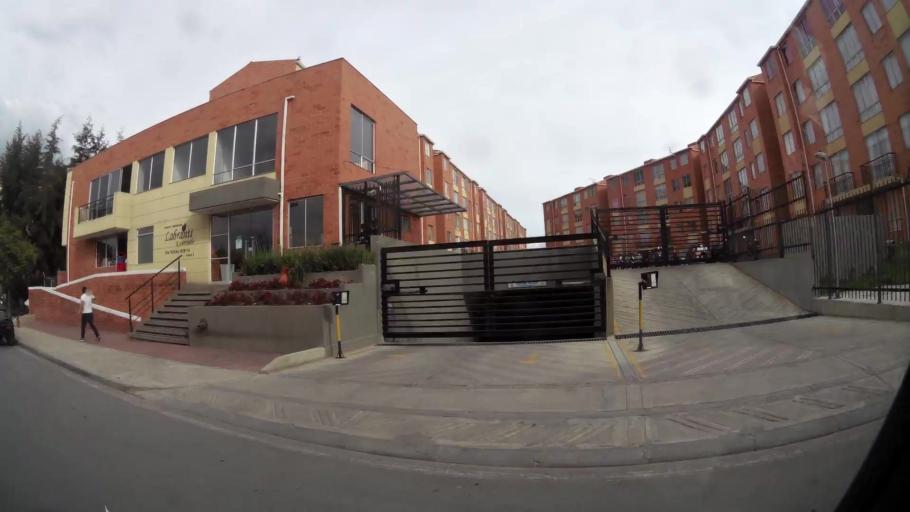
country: CO
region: Cundinamarca
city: Funza
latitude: 4.7028
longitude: -74.2113
